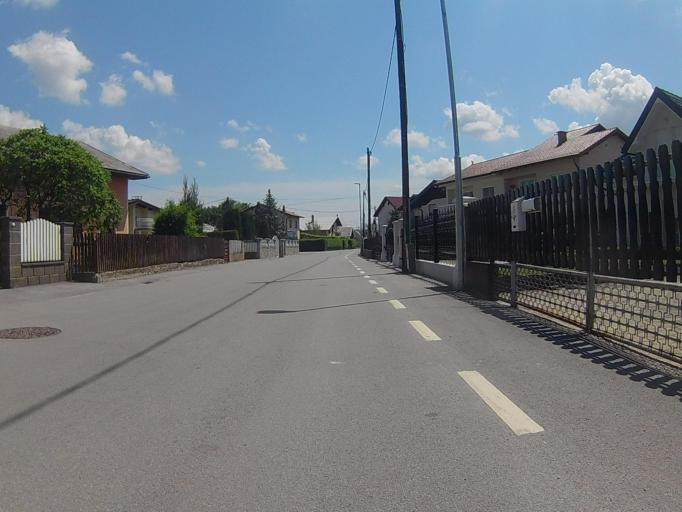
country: SI
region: Miklavz na Dravskem Polju
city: Miklavz na Dravskem Polju
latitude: 46.4830
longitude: 15.6992
